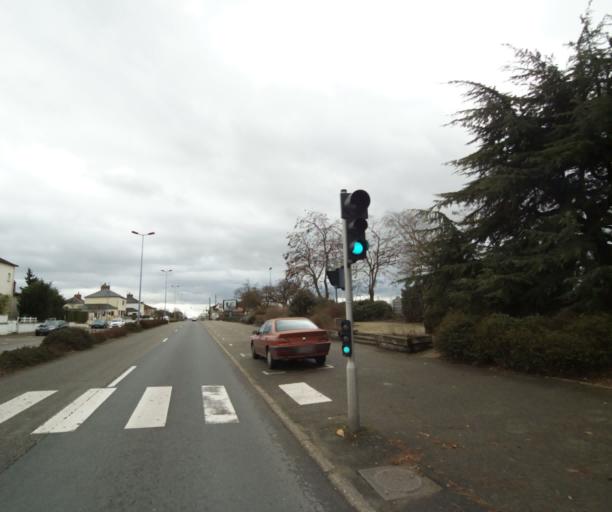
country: FR
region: Pays de la Loire
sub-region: Departement de la Sarthe
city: Le Mans
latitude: 47.9670
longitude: 0.2029
